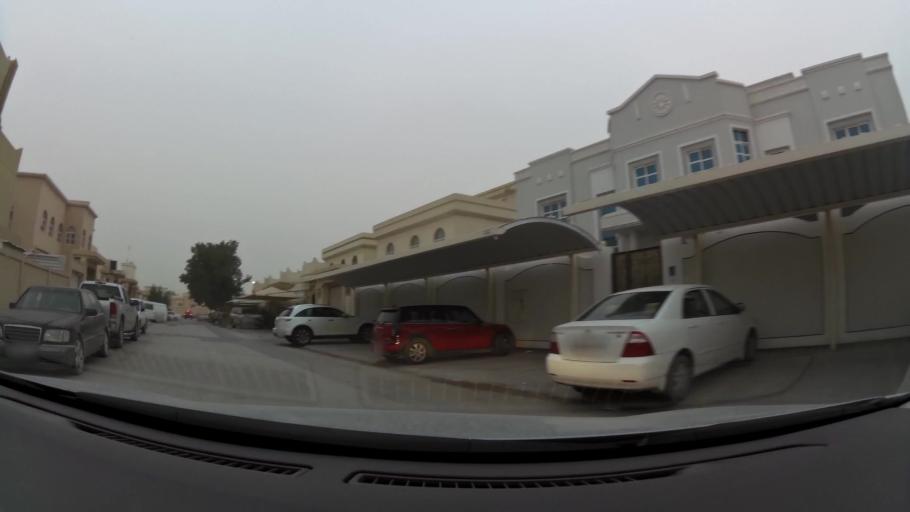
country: QA
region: Baladiyat ad Dawhah
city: Doha
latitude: 25.2369
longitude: 51.4974
